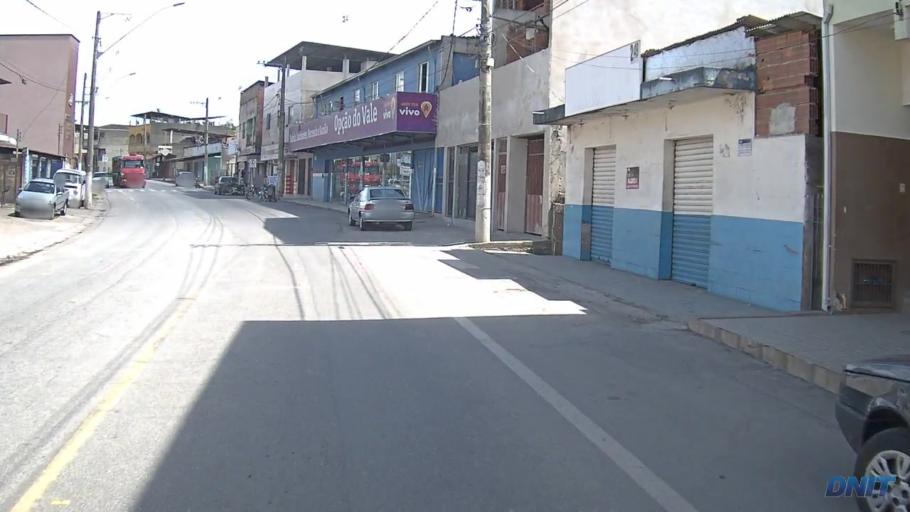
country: BR
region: Minas Gerais
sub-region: Coronel Fabriciano
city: Coronel Fabriciano
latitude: -19.5310
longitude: -42.6661
